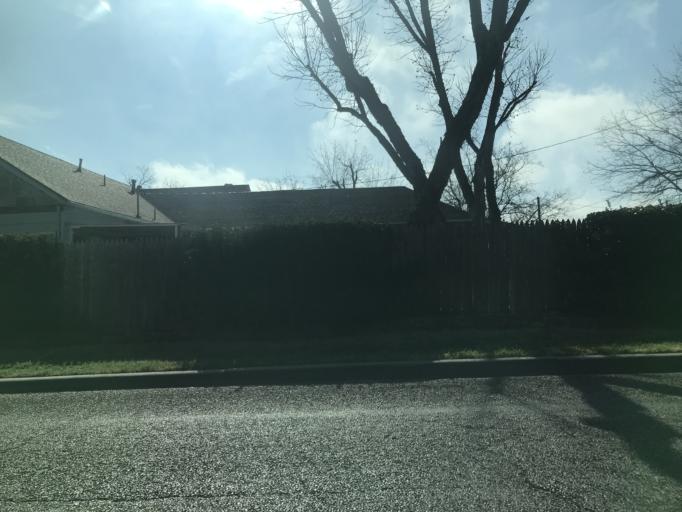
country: US
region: Texas
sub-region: Tom Green County
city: San Angelo
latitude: 31.4519
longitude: -100.4541
